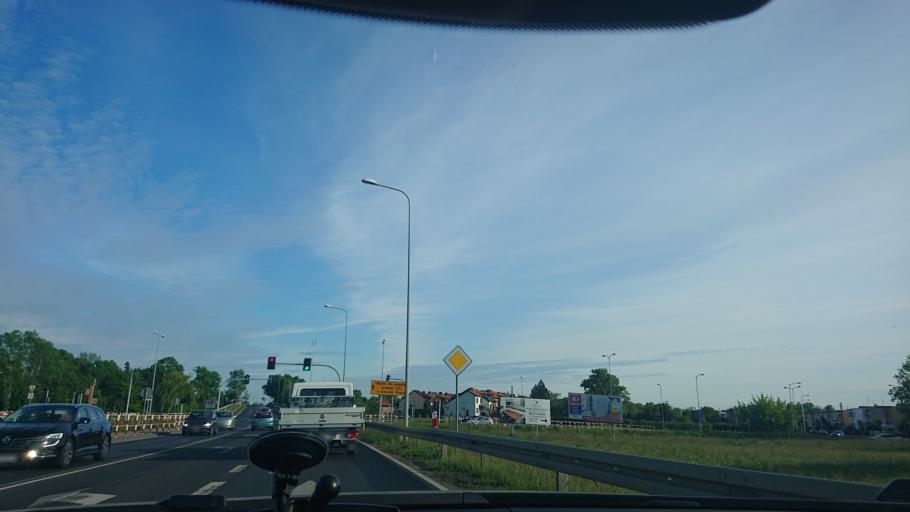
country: PL
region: Greater Poland Voivodeship
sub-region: Powiat gnieznienski
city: Gniezno
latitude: 52.5300
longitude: 17.5830
